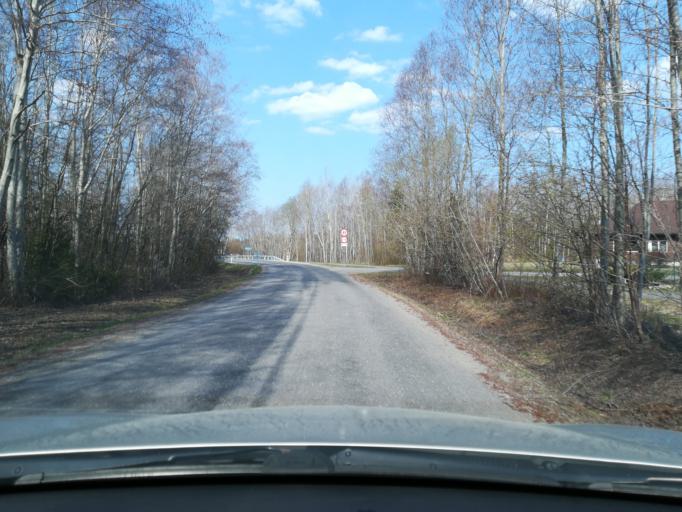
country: EE
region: Harju
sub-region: Saue linn
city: Saue
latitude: 59.3552
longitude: 24.5727
